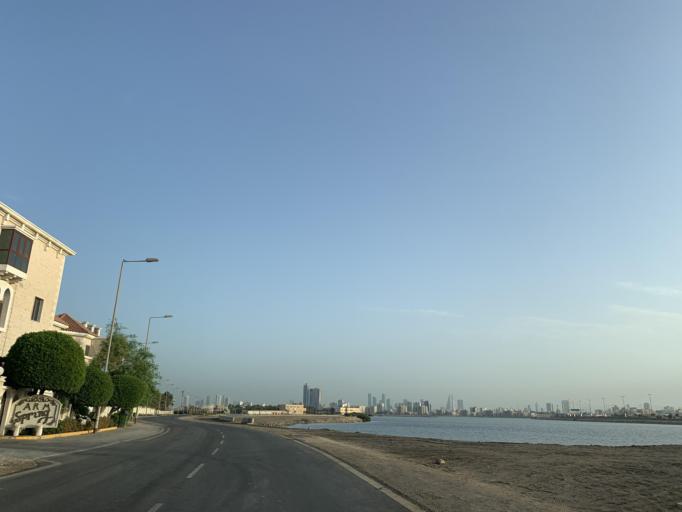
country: BH
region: Manama
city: Manama
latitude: 26.1845
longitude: 50.5879
